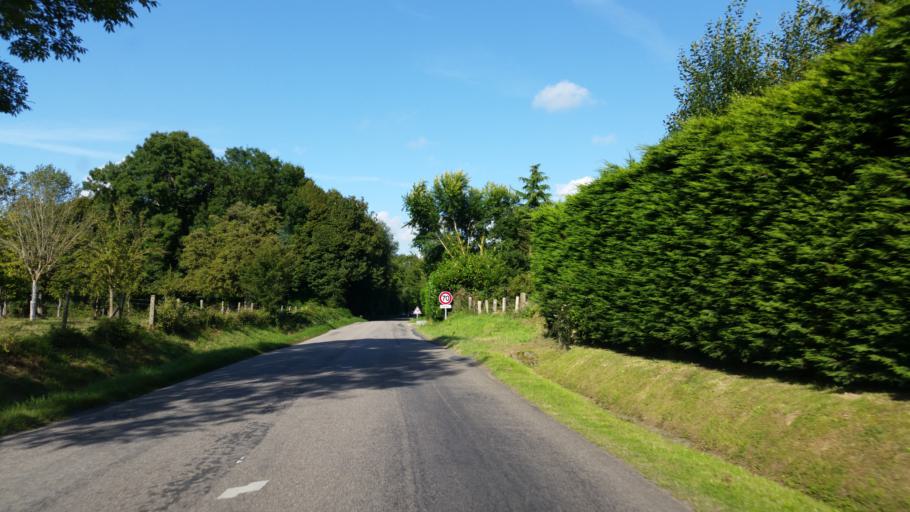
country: FR
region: Lower Normandy
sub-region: Departement du Calvados
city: Saint-Gatien-des-Bois
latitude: 49.3583
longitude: 0.1797
